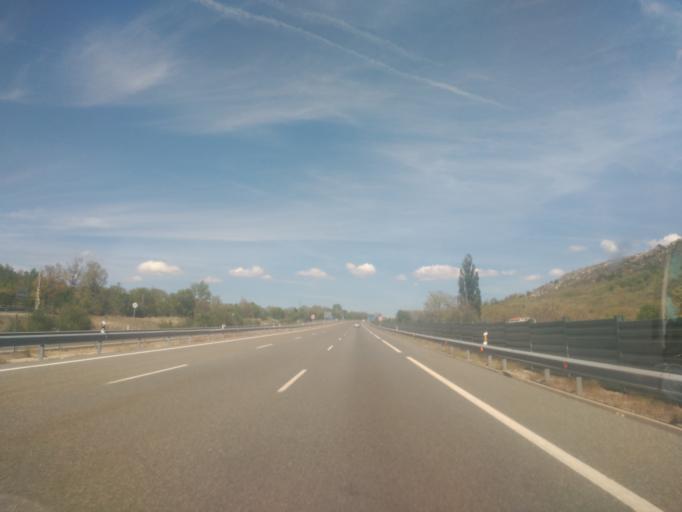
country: ES
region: Castille and Leon
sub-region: Provincia de Salamanca
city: Vallejera de Riofrio
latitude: 40.4152
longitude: -5.7157
